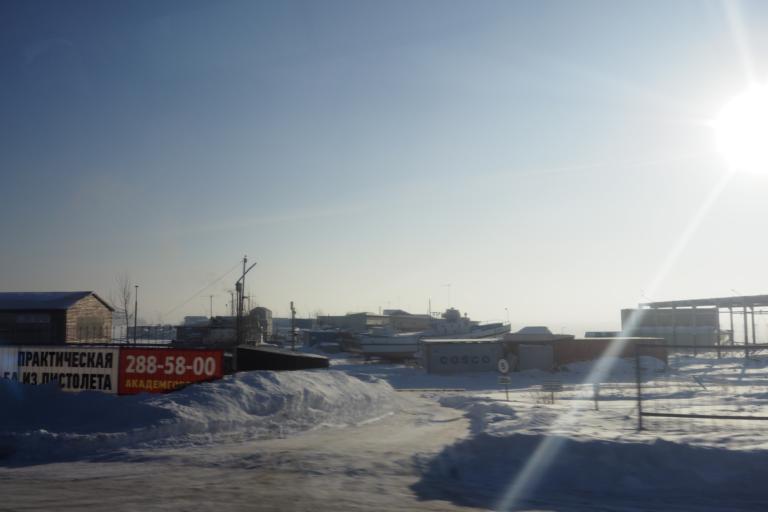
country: RU
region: Novosibirsk
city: Akademgorodok
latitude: 54.8422
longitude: 83.0333
